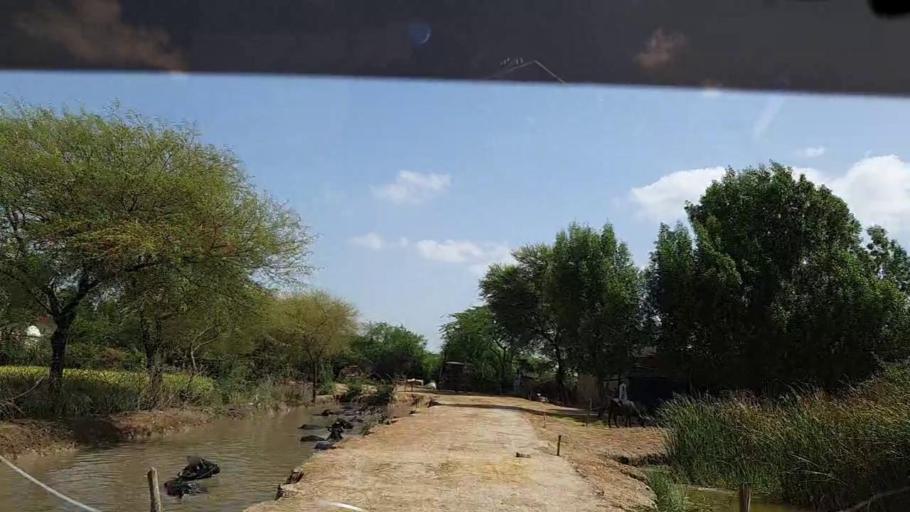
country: PK
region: Sindh
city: Badin
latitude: 24.5887
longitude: 68.8047
